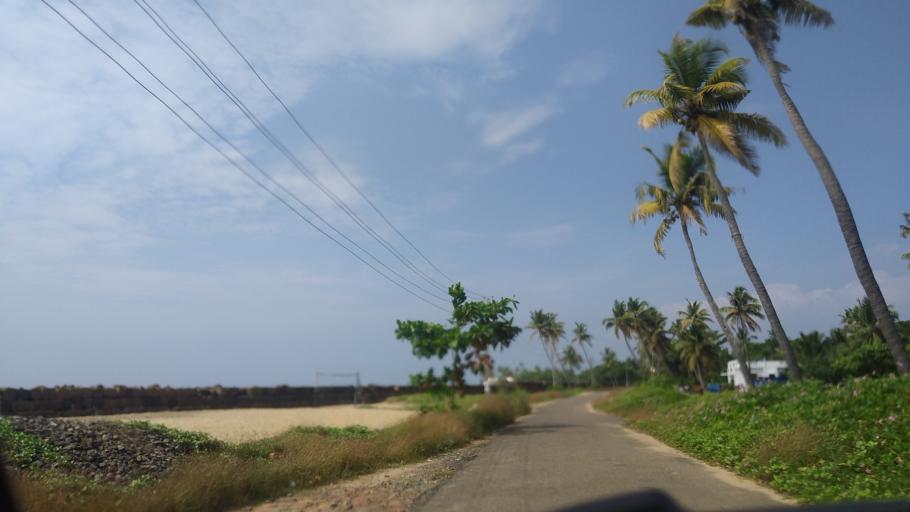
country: IN
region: Kerala
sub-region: Ernakulam
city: Elur
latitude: 10.0485
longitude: 76.2052
